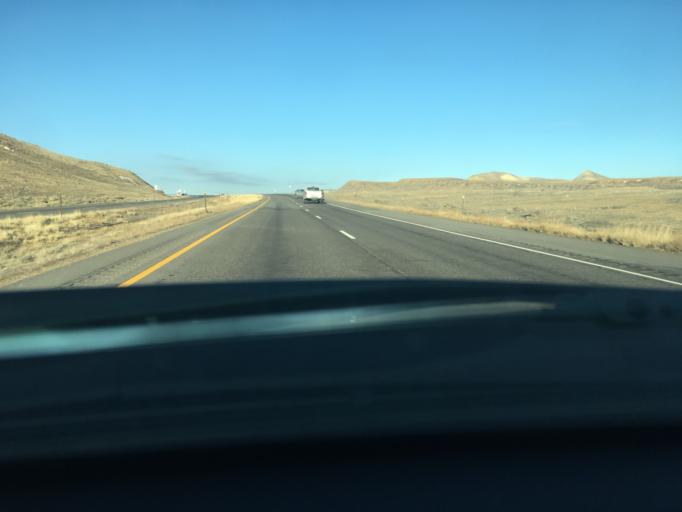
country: US
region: Colorado
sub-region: Delta County
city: Delta
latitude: 38.7539
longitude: -108.1700
